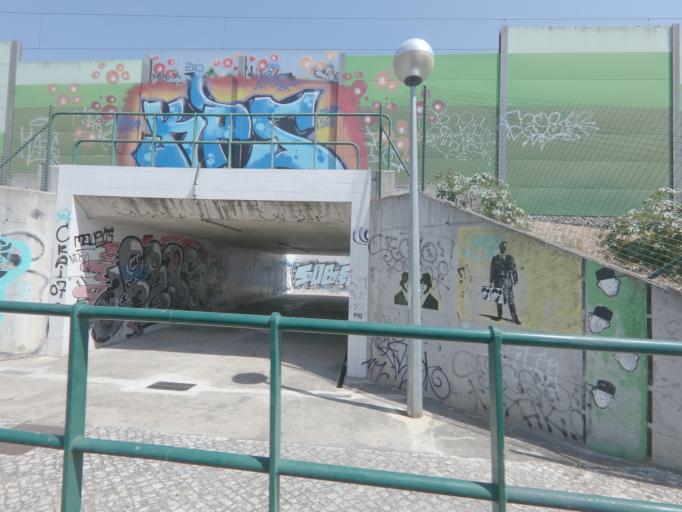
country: PT
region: Setubal
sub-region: Setubal
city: Setubal
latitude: 38.5388
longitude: -8.8830
